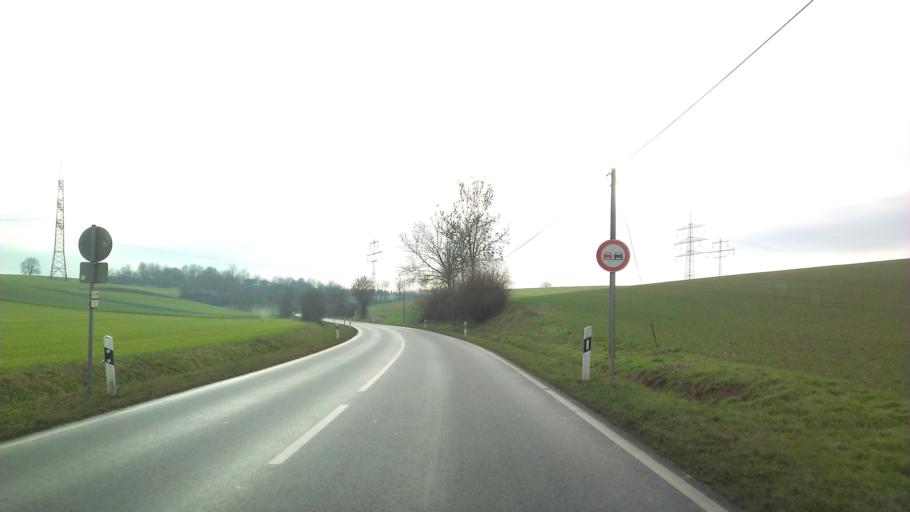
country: DE
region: Baden-Wuerttemberg
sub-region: Karlsruhe Region
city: Meckesheim
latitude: 49.3135
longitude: 8.8052
